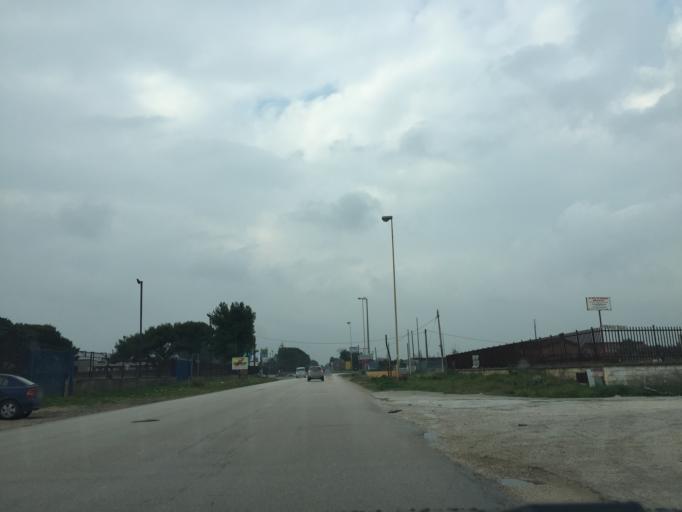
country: IT
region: Apulia
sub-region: Provincia di Foggia
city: Foggia
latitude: 41.4441
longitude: 15.5019
